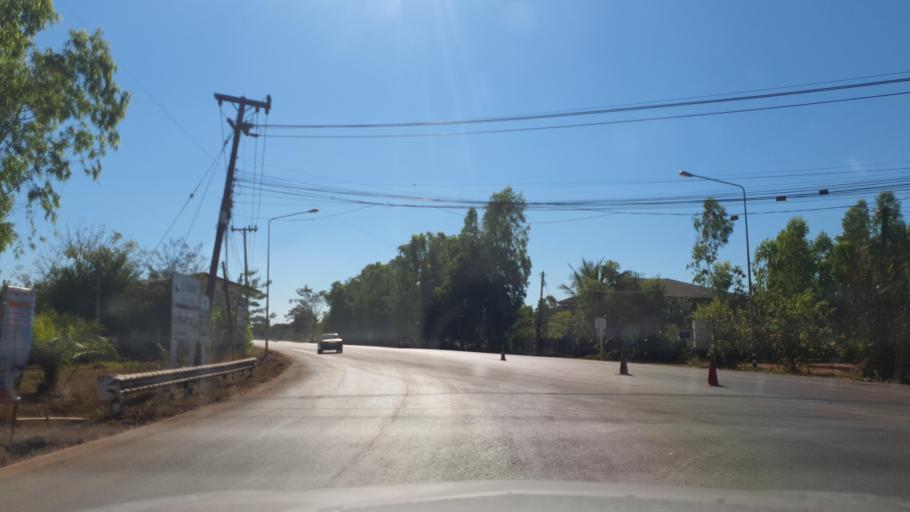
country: TH
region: Nakhon Phanom
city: Si Songkhram
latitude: 17.7658
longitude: 104.2783
